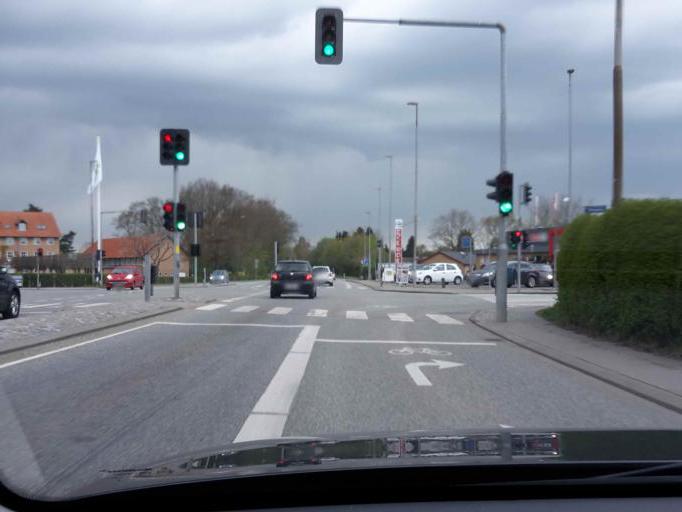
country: DK
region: South Denmark
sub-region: Odense Kommune
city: Odense
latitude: 55.4118
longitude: 10.3285
